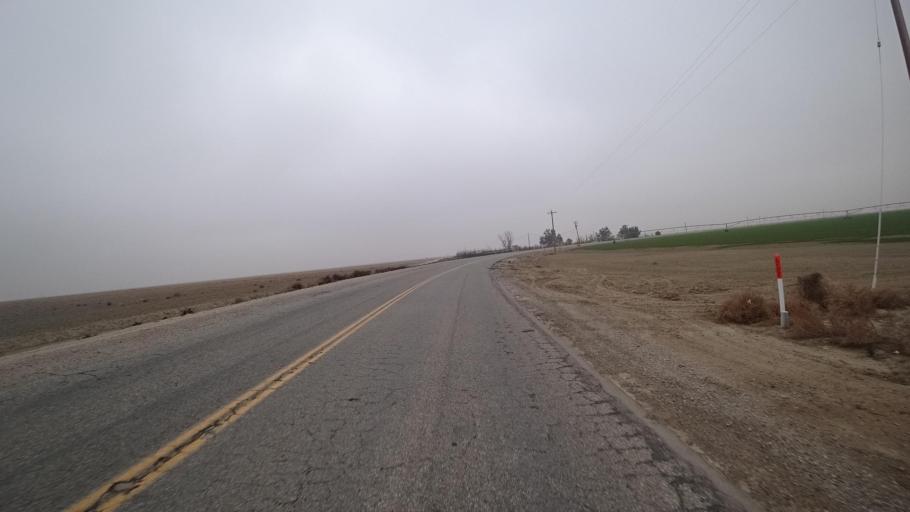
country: US
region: California
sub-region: Kern County
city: Maricopa
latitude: 35.1554
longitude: -119.1989
